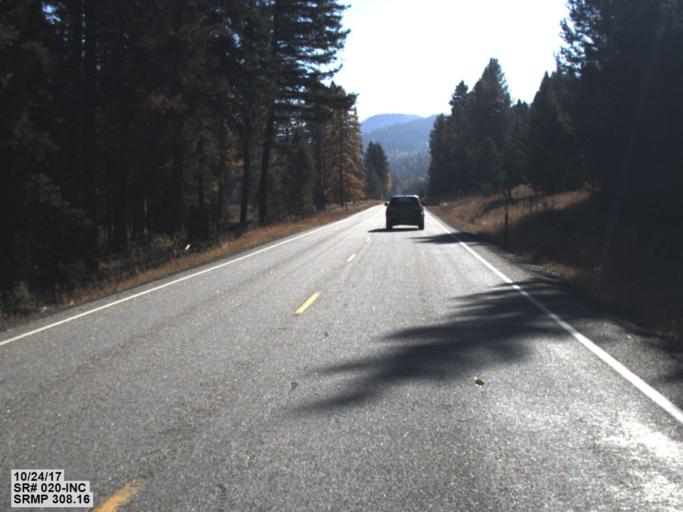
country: US
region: Washington
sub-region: Ferry County
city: Republic
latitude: 48.6125
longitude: -118.6635
